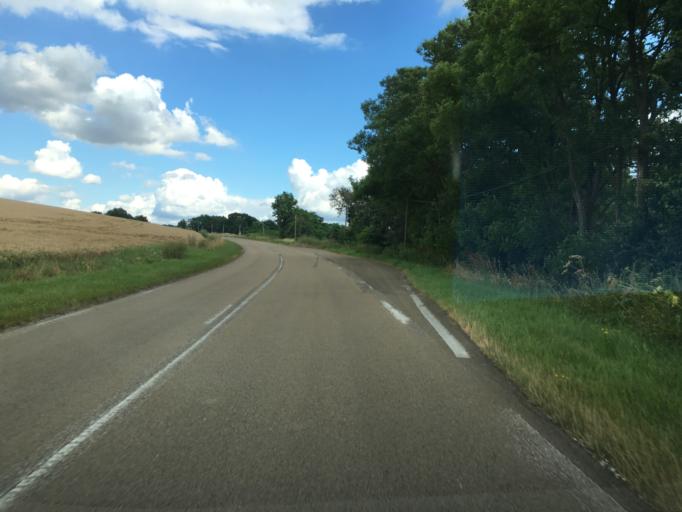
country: FR
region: Bourgogne
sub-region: Departement de l'Yonne
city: Charbuy
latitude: 47.8242
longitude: 3.4251
